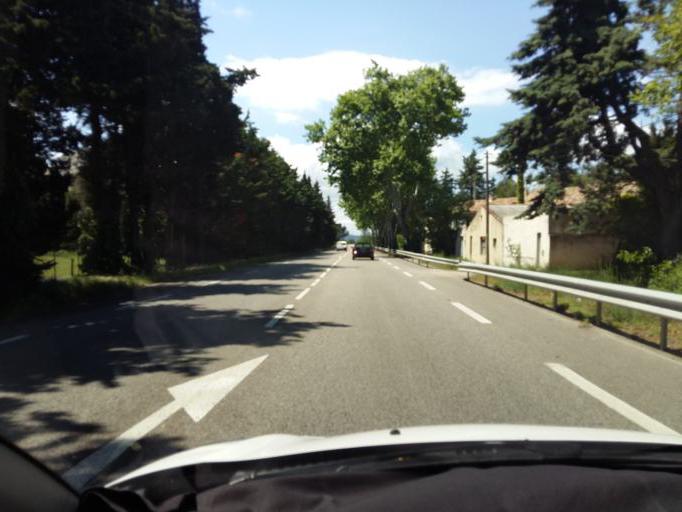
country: FR
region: Provence-Alpes-Cote d'Azur
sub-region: Departement des Bouches-du-Rhone
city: Alleins
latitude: 43.7354
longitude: 5.1318
